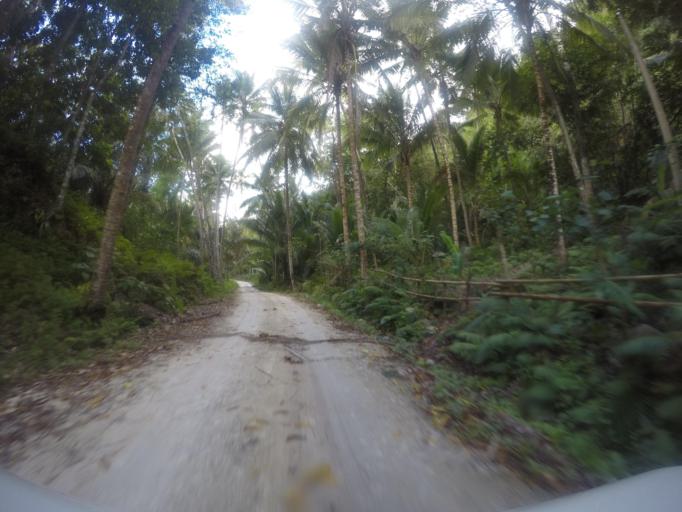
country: TL
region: Lautem
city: Lospalos
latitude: -8.5282
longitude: 126.9349
